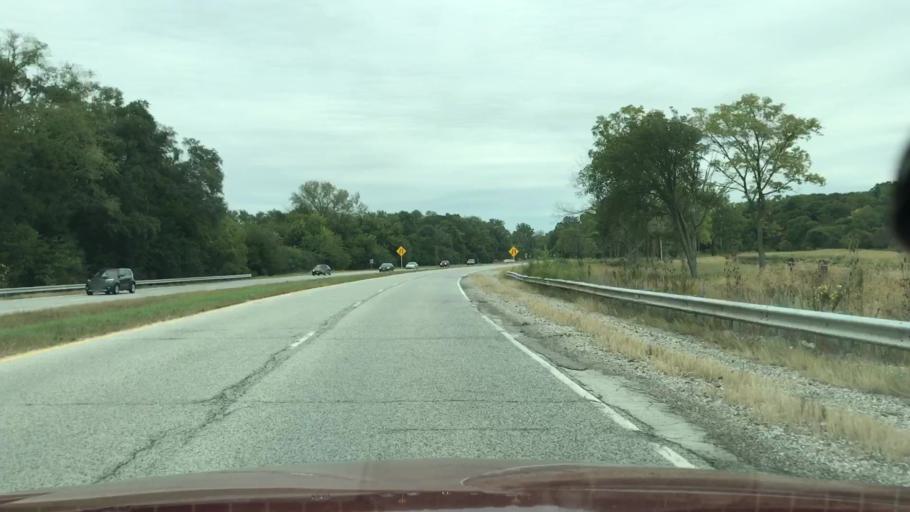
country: US
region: Illinois
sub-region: DuPage County
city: Lisle
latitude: 41.8186
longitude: -88.0693
